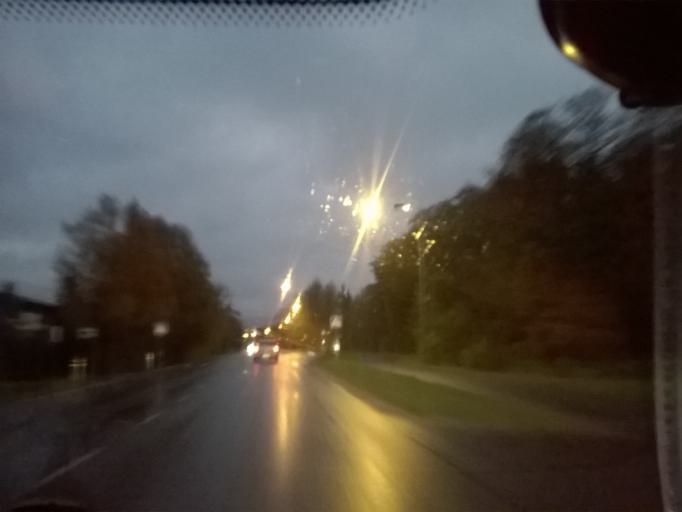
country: EE
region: Harju
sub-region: Viimsi vald
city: Rummu
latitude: 59.5222
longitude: 24.8032
